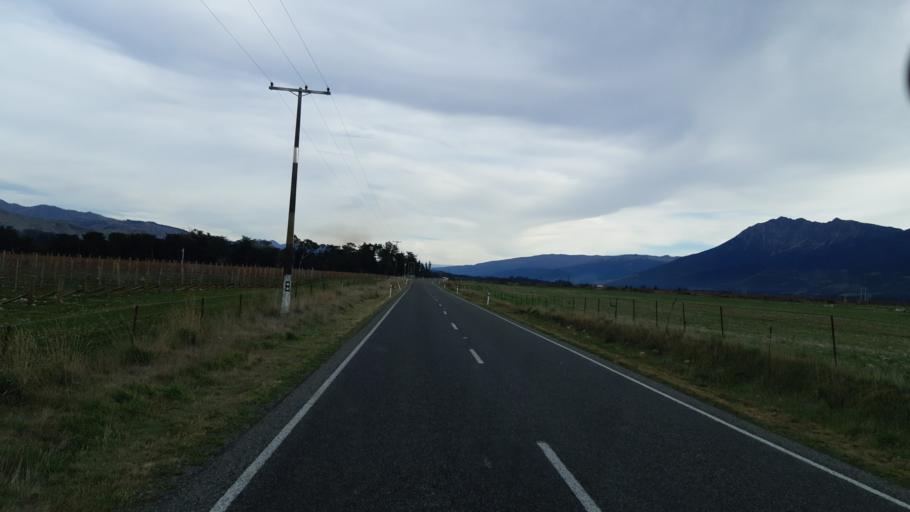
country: NZ
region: Tasman
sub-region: Tasman District
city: Richmond
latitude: -41.6161
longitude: 173.3799
